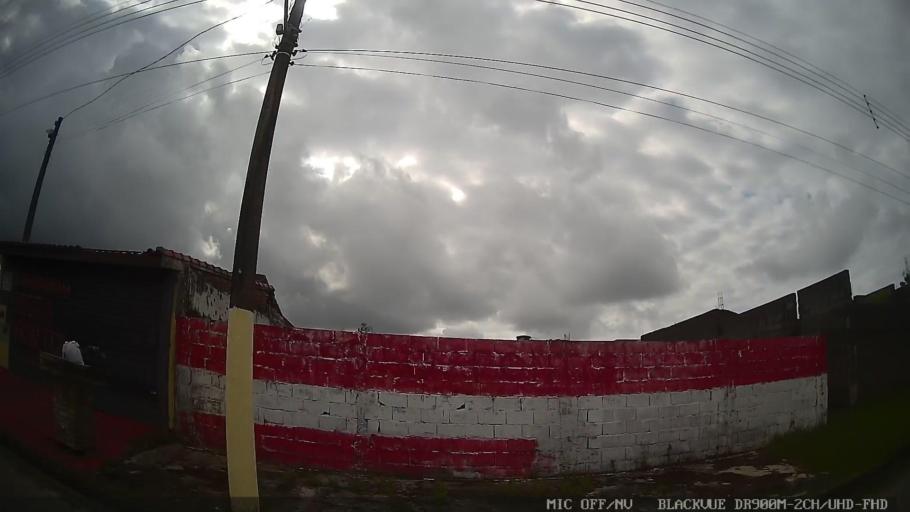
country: BR
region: Sao Paulo
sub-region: Itanhaem
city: Itanhaem
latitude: -24.1928
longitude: -46.8245
